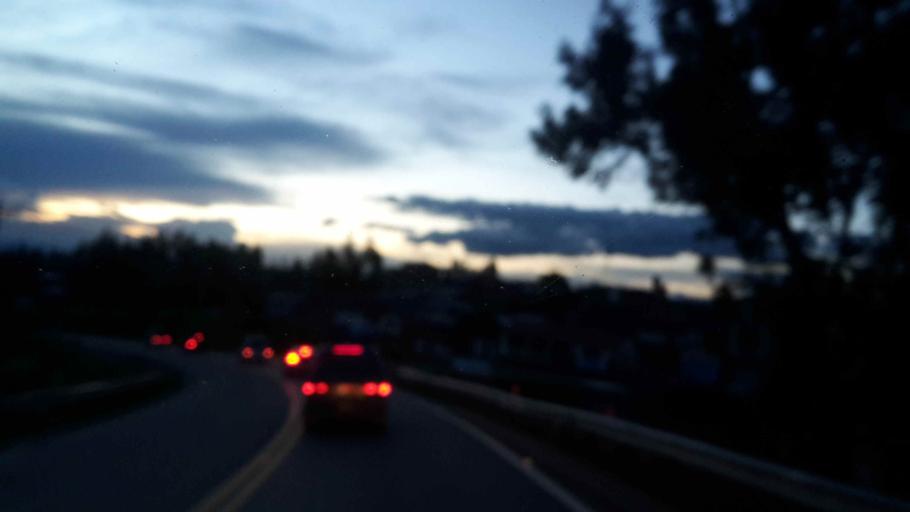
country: BO
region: Cochabamba
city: Colomi
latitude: -17.4193
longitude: -65.9250
